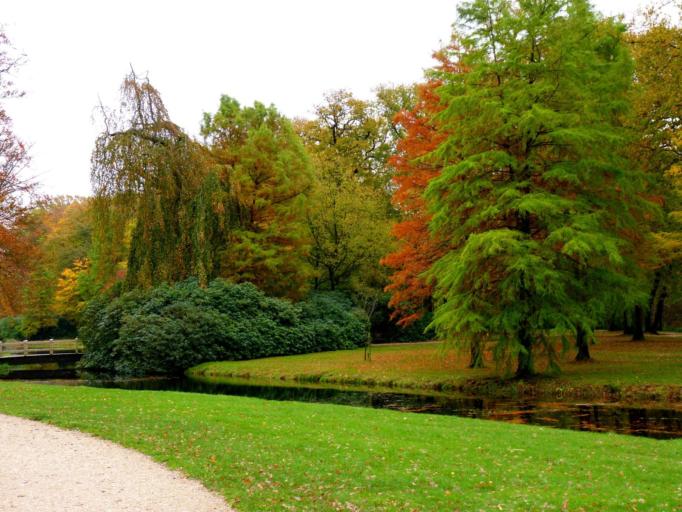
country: NL
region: Utrecht
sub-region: Gemeente Baarn
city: Baarn
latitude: 52.2171
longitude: 5.2475
